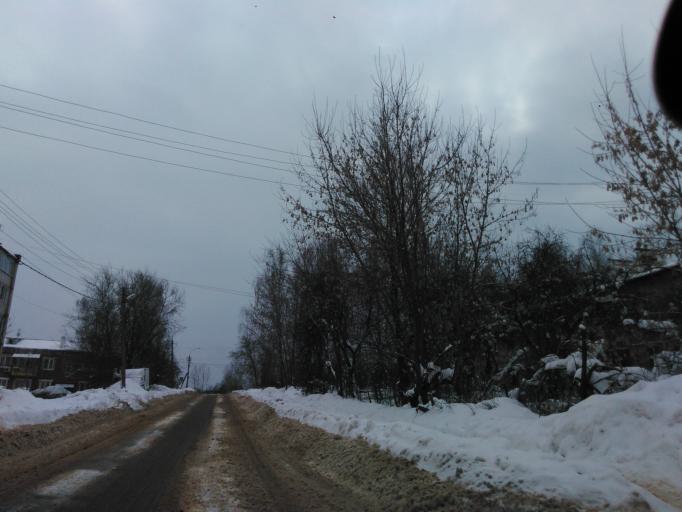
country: RU
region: Moskovskaya
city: Yakhroma
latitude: 56.2769
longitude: 37.4834
